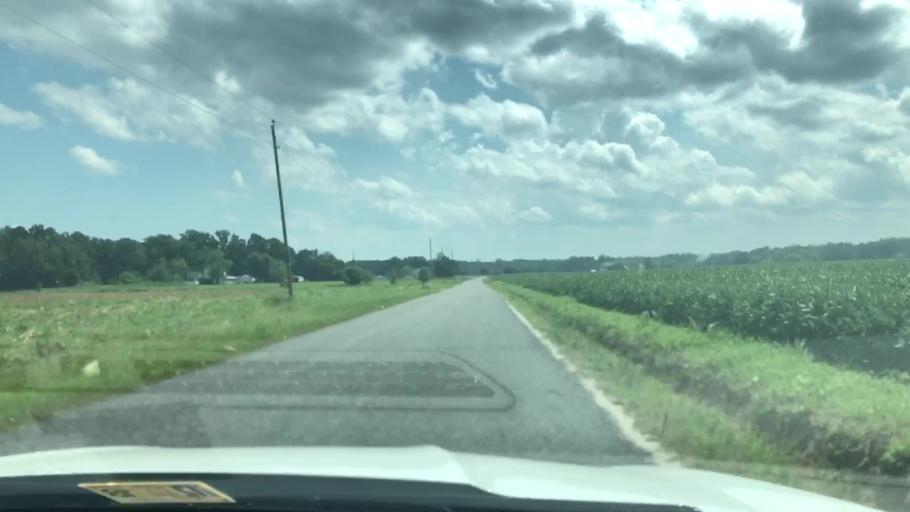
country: US
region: Virginia
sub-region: Middlesex County
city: Saluda
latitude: 37.6513
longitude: -76.6812
